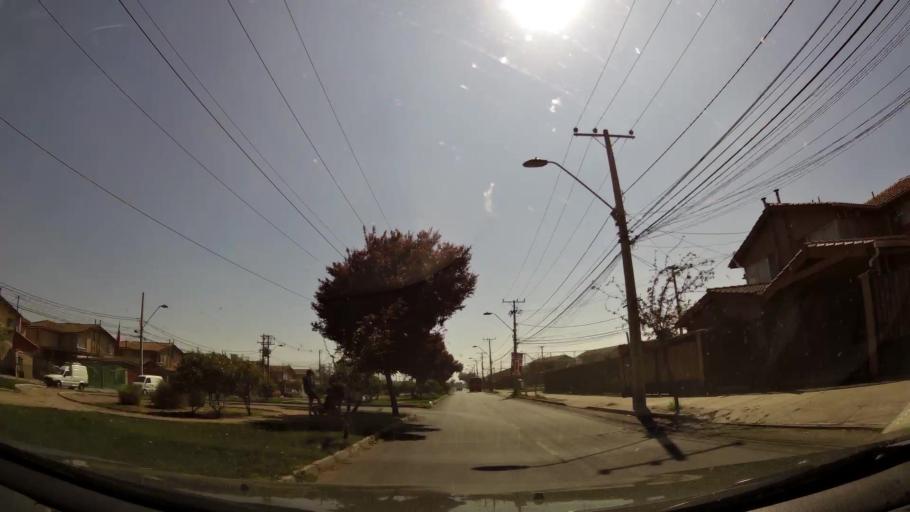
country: CL
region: Santiago Metropolitan
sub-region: Provincia de Santiago
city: Lo Prado
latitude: -33.3528
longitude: -70.7365
